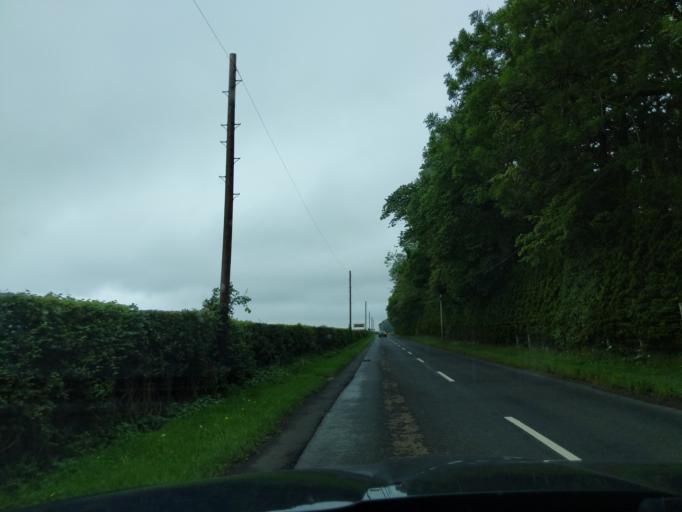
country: GB
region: England
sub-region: Northumberland
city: Lowick
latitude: 55.6488
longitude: -2.0093
